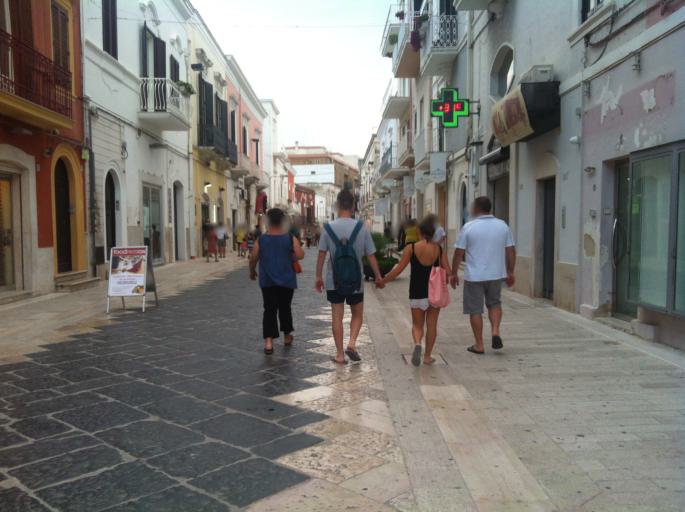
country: IT
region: Apulia
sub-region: Provincia di Foggia
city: Manfredonia
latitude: 41.6301
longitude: 15.9202
